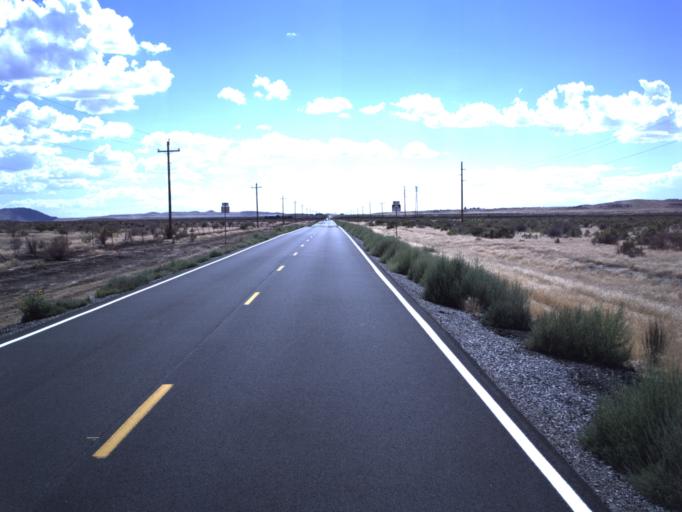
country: US
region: Utah
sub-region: Tooele County
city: Grantsville
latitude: 40.2648
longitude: -112.6877
